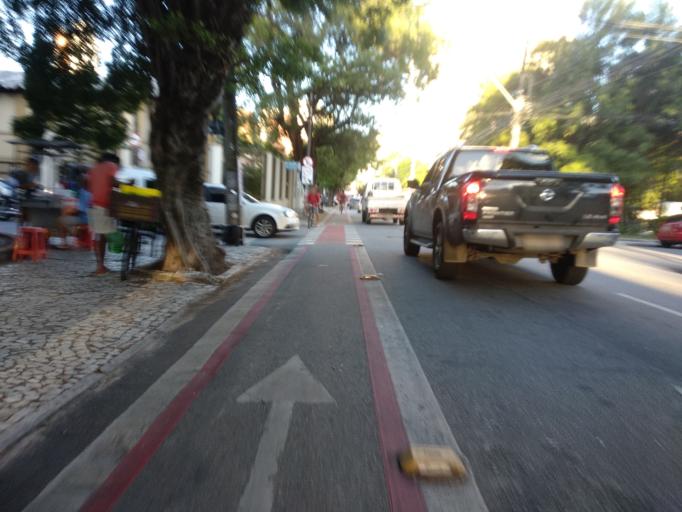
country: BR
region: Ceara
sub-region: Fortaleza
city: Fortaleza
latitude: -3.7318
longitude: -38.5117
